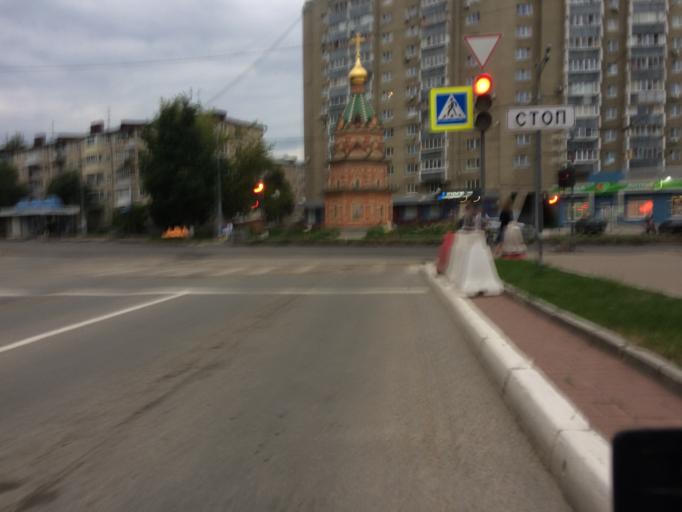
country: RU
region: Mariy-El
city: Yoshkar-Ola
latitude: 56.6300
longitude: 47.8822
